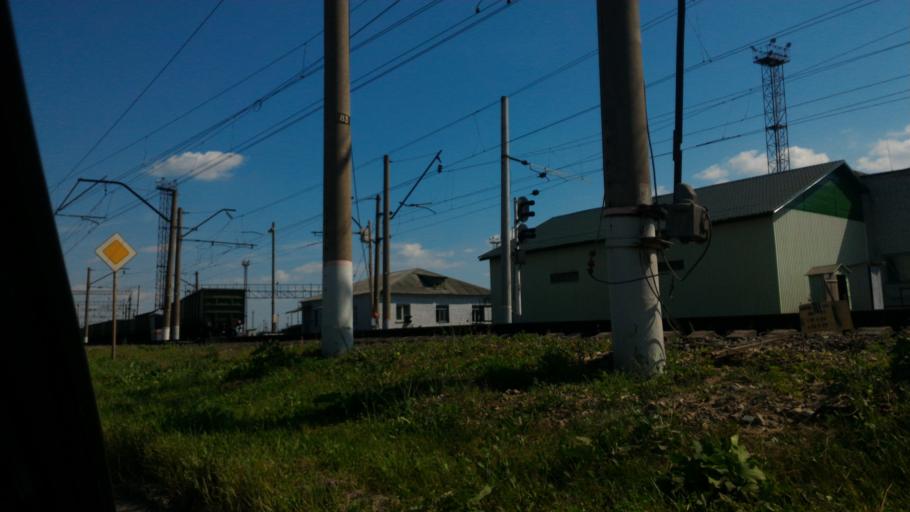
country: RU
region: Rjazan
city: Rybnoye
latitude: 54.7298
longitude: 39.5082
